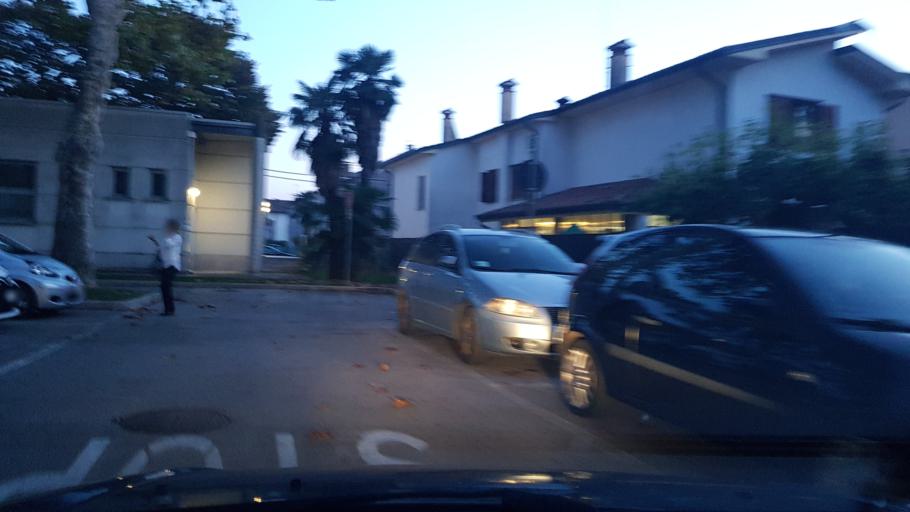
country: IT
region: Friuli Venezia Giulia
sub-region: Provincia di Gorizia
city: Staranzano
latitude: 45.8066
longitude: 13.4994
